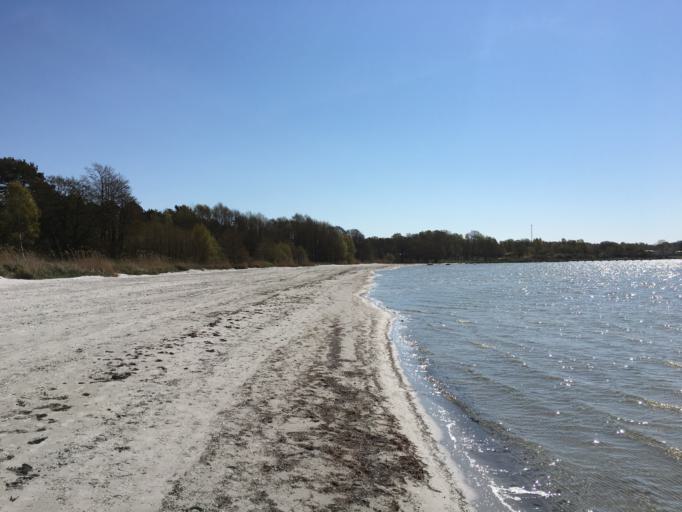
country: SE
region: Blekinge
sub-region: Solvesborgs Kommun
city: Soelvesborg
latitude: 56.0193
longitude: 14.6052
